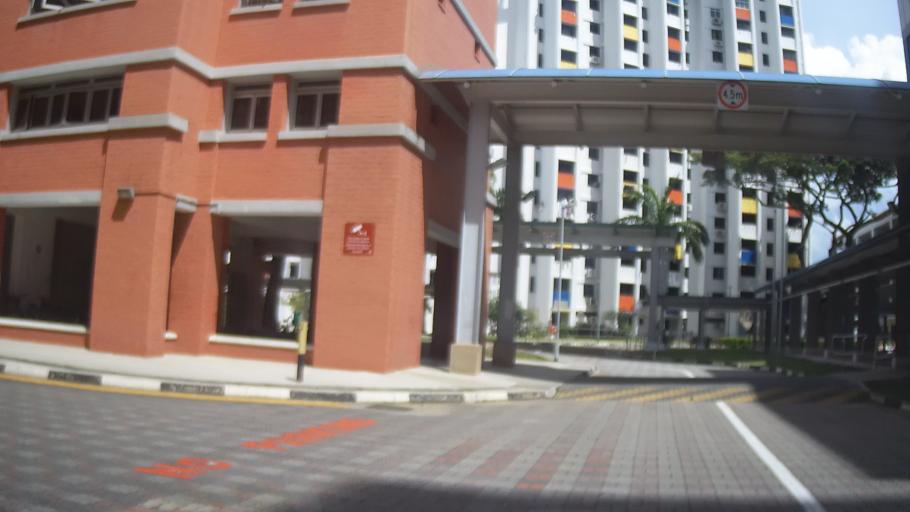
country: SG
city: Singapore
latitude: 1.3298
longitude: 103.8860
